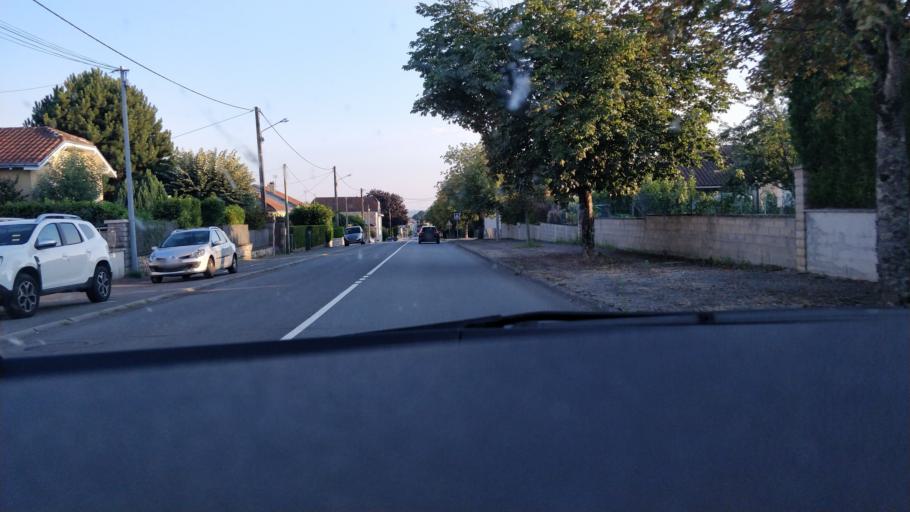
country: FR
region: Limousin
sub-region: Departement de la Haute-Vienne
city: Couzeix
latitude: 45.8820
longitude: 1.2385
